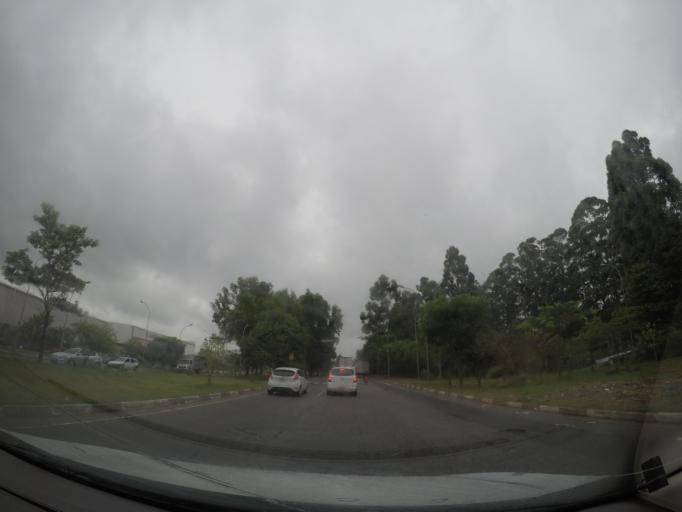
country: BR
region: Sao Paulo
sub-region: Guarulhos
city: Guarulhos
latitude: -23.4305
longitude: -46.4944
